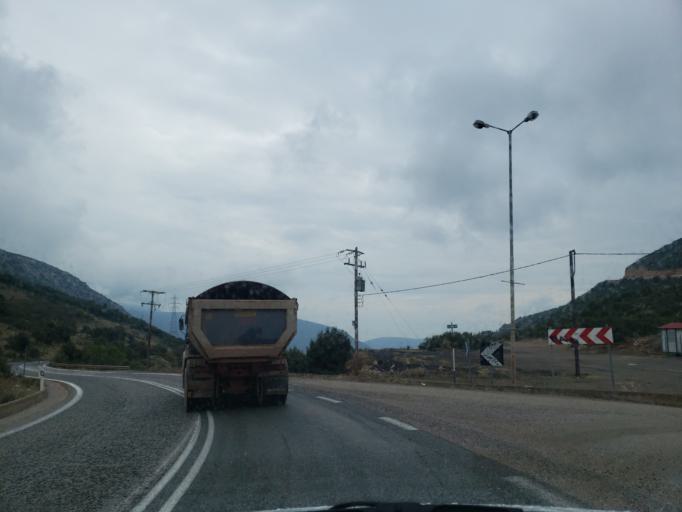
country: GR
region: Central Greece
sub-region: Nomos Fokidos
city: Amfissa
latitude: 38.5698
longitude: 22.3967
